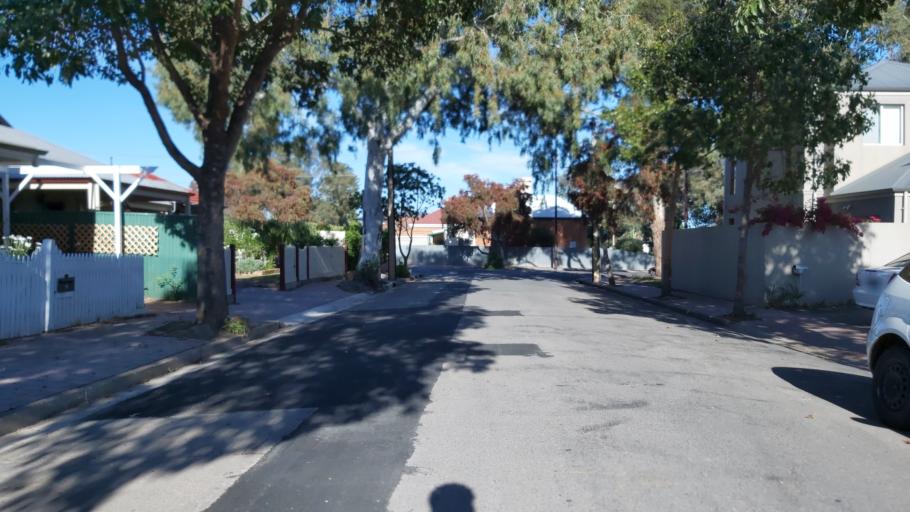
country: AU
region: South Australia
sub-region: Unley
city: Fullarton
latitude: -34.9504
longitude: 138.6240
